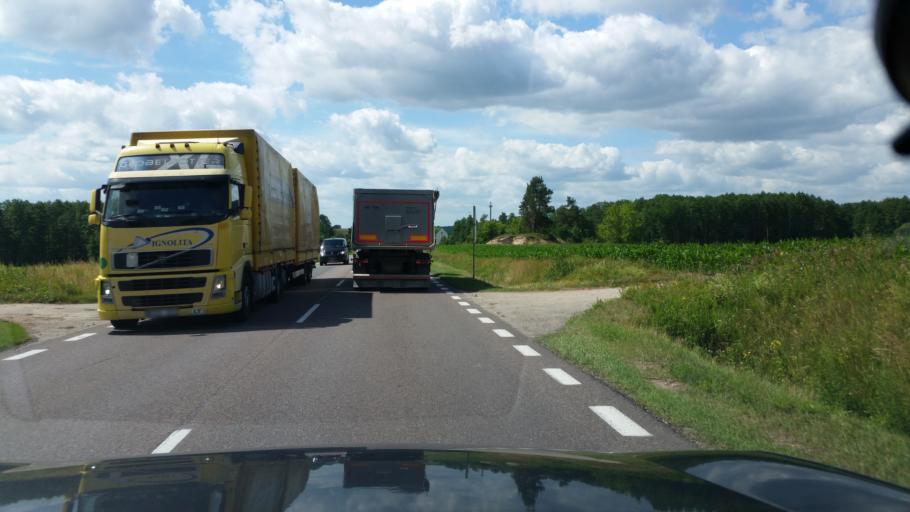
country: PL
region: Podlasie
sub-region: Powiat grajewski
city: Szczuczyn
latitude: 53.5161
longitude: 22.2470
